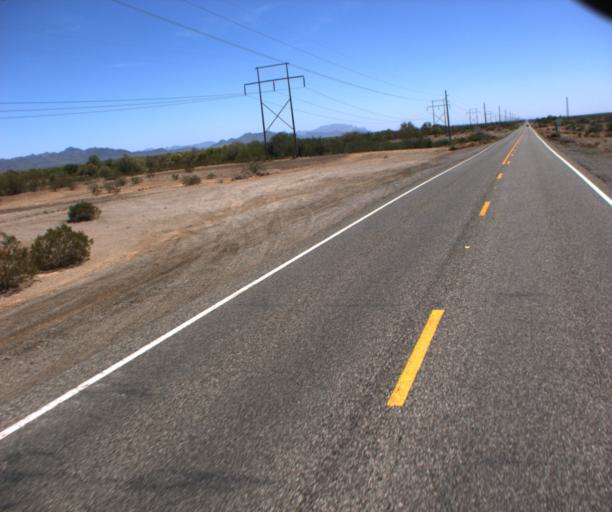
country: US
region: Arizona
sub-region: La Paz County
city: Quartzsite
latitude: 33.7254
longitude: -114.2171
